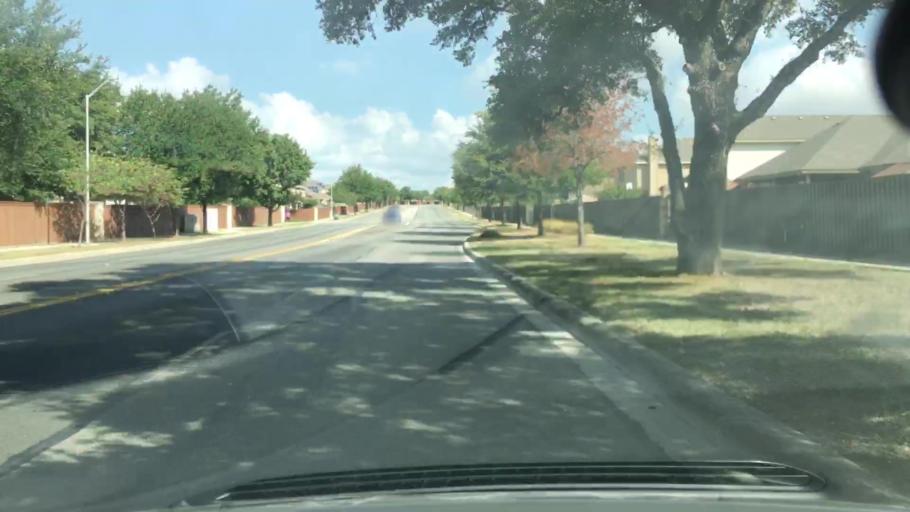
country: US
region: Texas
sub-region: Guadalupe County
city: Cibolo
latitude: 29.5774
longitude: -98.2441
